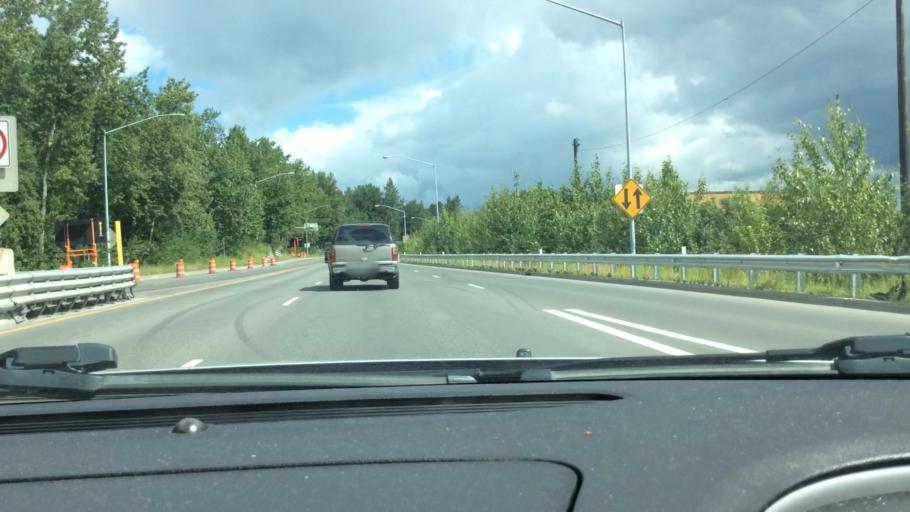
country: US
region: Alaska
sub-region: Anchorage Municipality
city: Anchorage
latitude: 61.2273
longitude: -149.8832
